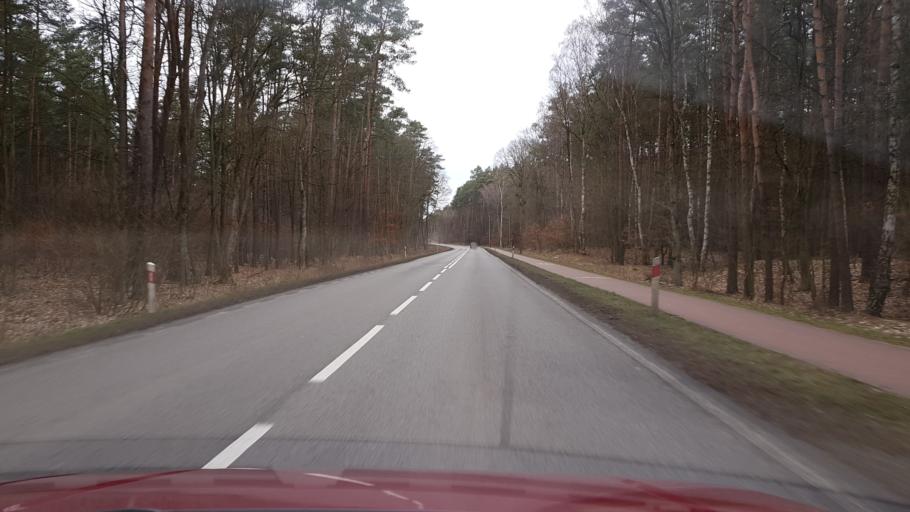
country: PL
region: West Pomeranian Voivodeship
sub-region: Powiat policki
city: Dobra
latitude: 53.5122
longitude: 14.4748
